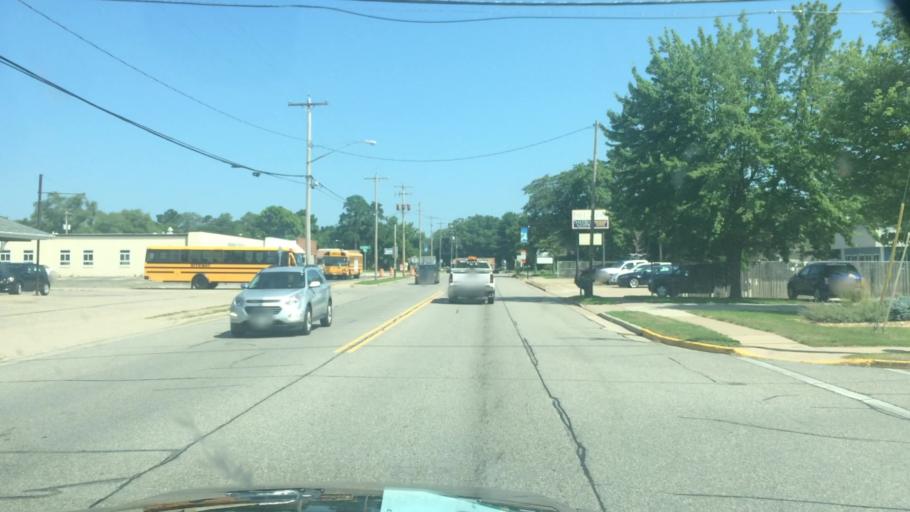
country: US
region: Wisconsin
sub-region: Waupaca County
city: Waupaca
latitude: 44.3486
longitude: -89.0721
